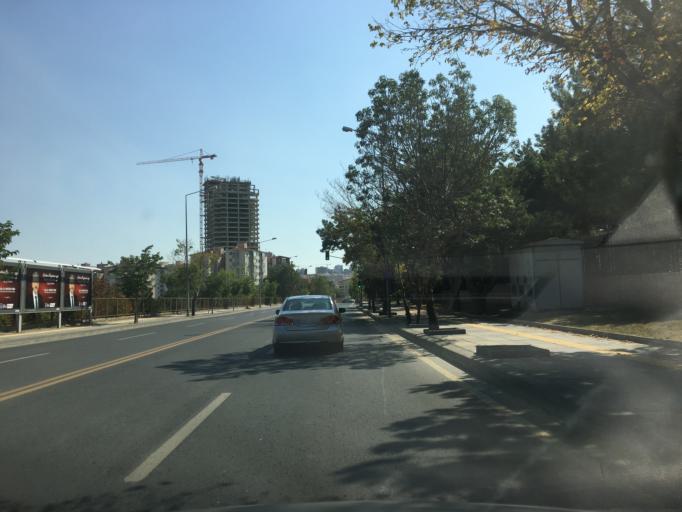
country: TR
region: Ankara
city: Cankaya
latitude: 39.8824
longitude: 32.8666
